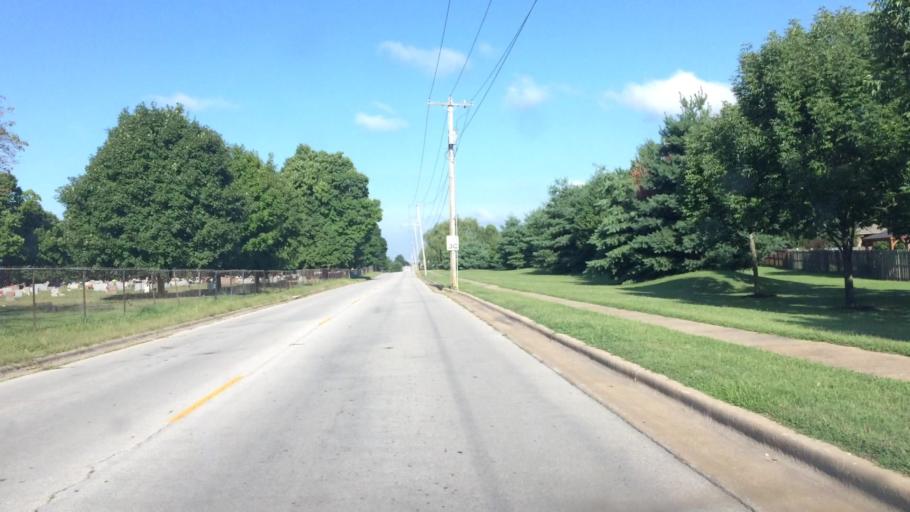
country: US
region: Missouri
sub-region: Greene County
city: Springfield
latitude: 37.2662
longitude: -93.2720
